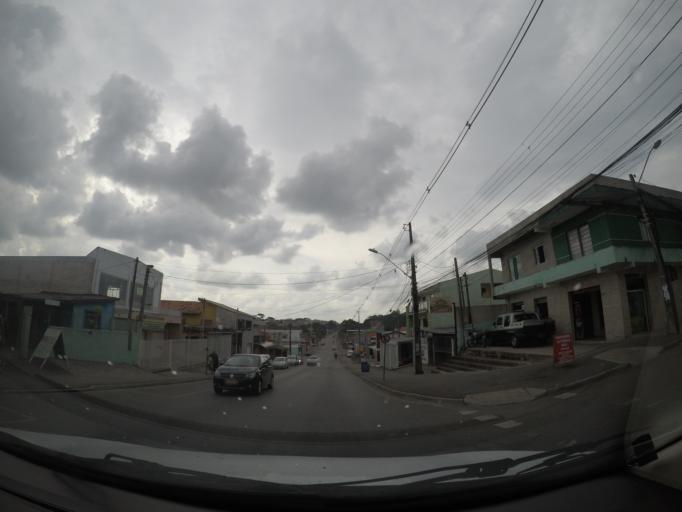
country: BR
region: Parana
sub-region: Sao Jose Dos Pinhais
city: Sao Jose dos Pinhais
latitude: -25.5498
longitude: -49.2473
